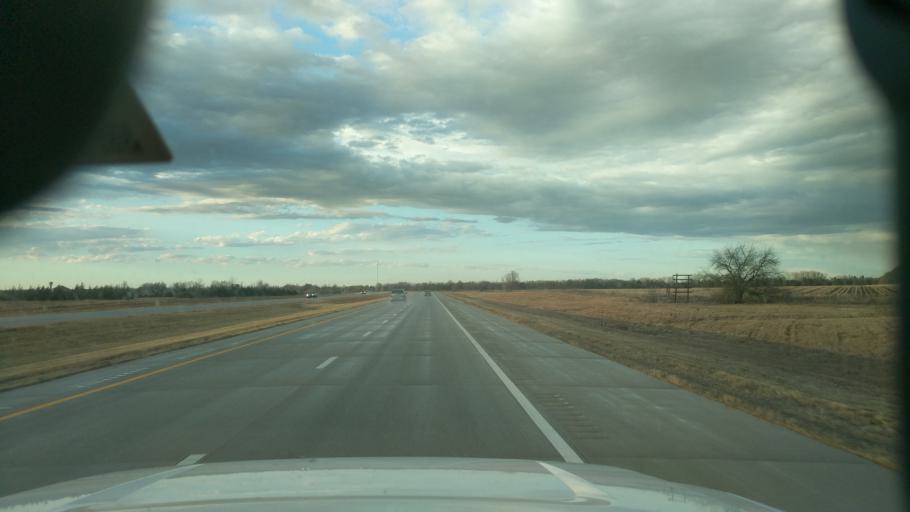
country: US
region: Kansas
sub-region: Harvey County
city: Hesston
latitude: 38.1290
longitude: -97.4001
